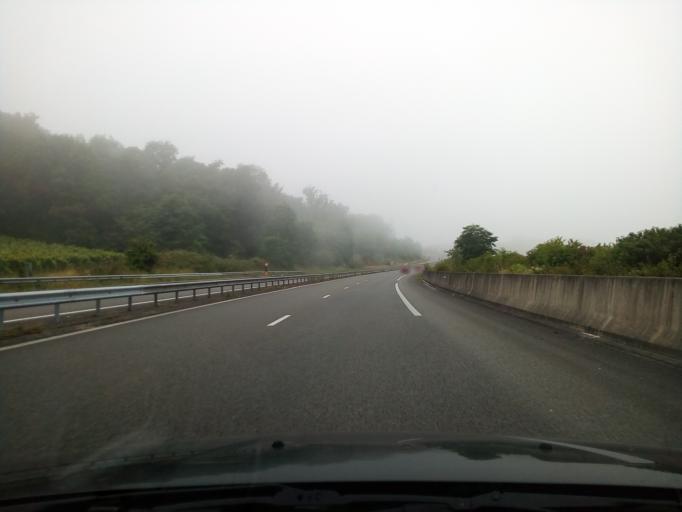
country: FR
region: Poitou-Charentes
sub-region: Departement de la Charente
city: Jarnac
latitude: 45.6668
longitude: -0.1796
